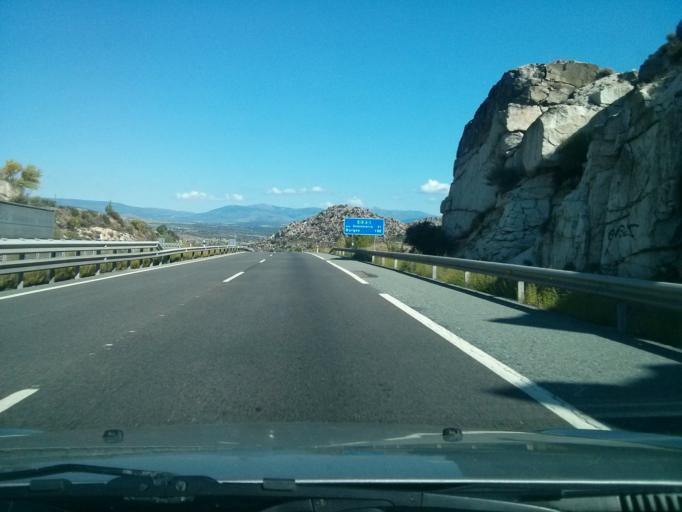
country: ES
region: Madrid
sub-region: Provincia de Madrid
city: La Cabrera
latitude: 40.8777
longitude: -3.5996
